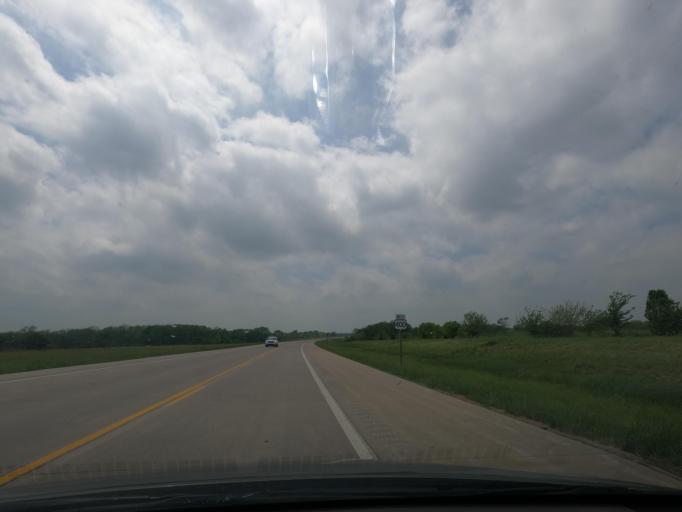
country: US
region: Kansas
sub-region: Labette County
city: Parsons
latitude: 37.3497
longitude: -95.3234
